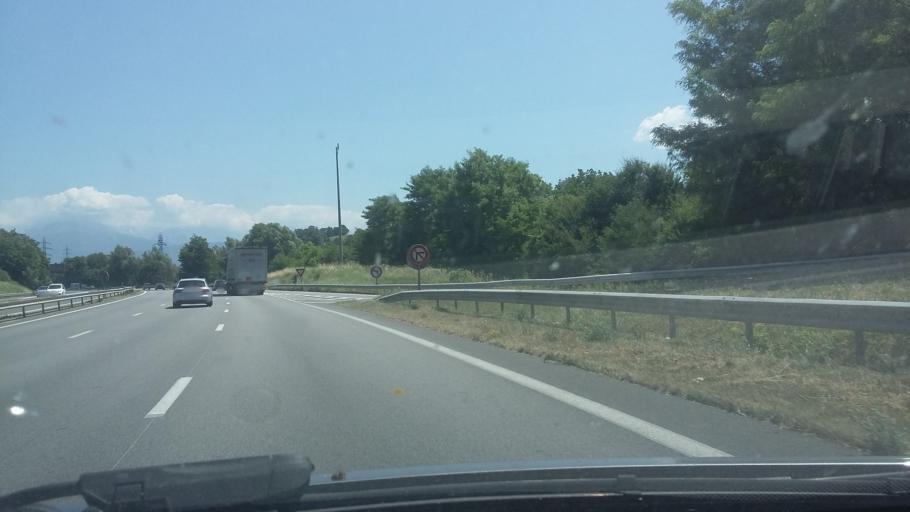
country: FR
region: Rhone-Alpes
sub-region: Departement de la Savoie
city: Chambery
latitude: 45.5587
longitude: 5.9492
